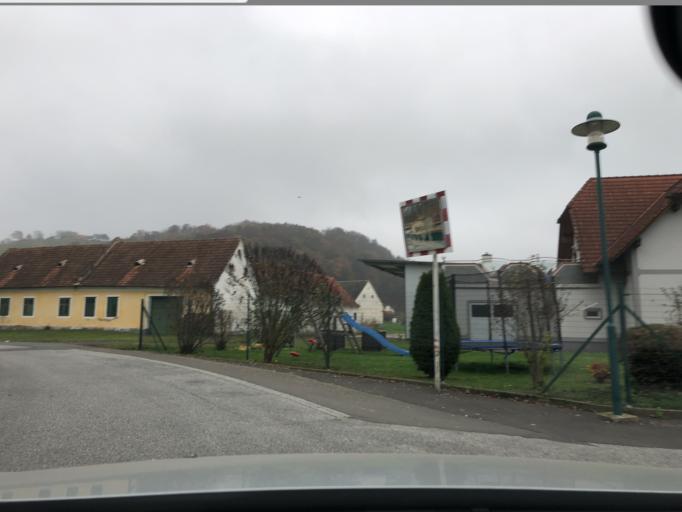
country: AT
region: Styria
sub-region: Politischer Bezirk Suedoststeiermark
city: Fehring
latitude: 46.9547
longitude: 16.0356
